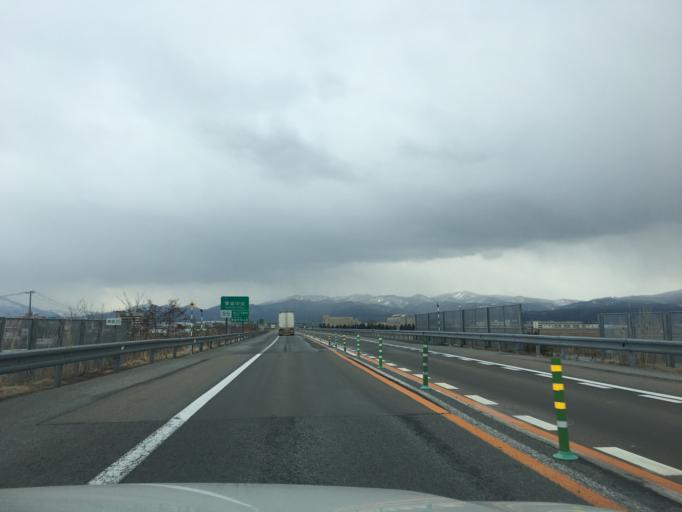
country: JP
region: Aomori
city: Aomori Shi
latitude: 40.7974
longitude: 140.7289
